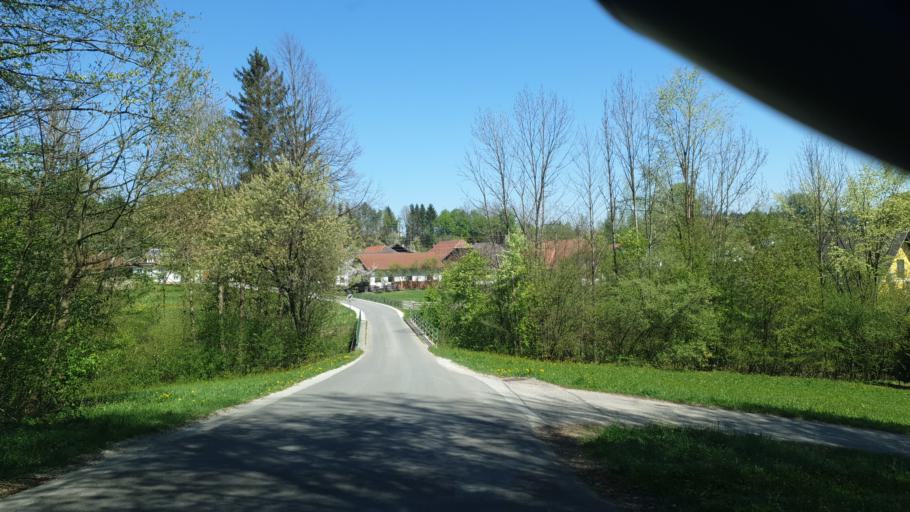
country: AT
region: Upper Austria
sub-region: Politischer Bezirk Vocklabruck
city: Gampern
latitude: 47.9945
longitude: 13.5590
